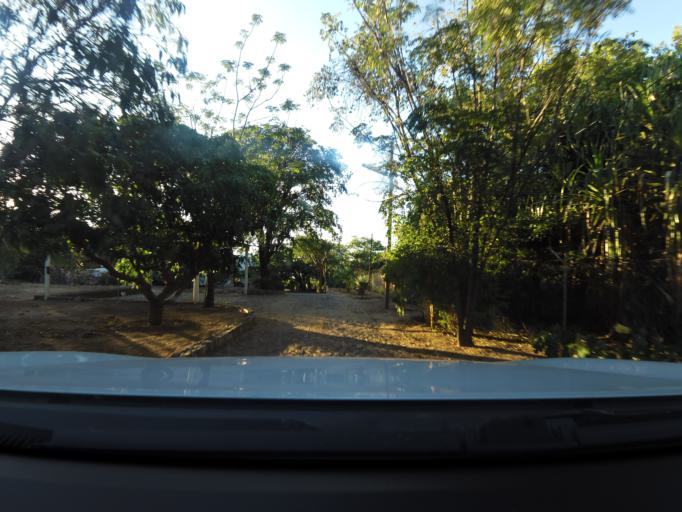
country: ZW
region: Matabeleland North
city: Binga
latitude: -17.6092
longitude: 27.3501
